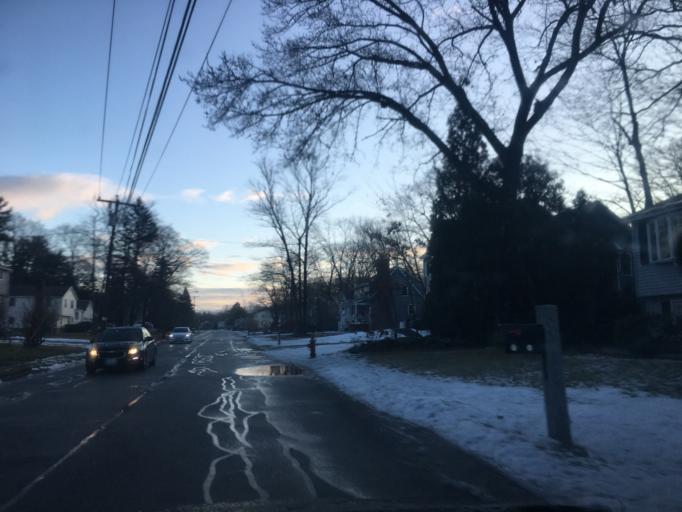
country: US
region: Massachusetts
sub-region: Middlesex County
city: Billerica
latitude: 42.5466
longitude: -71.2696
